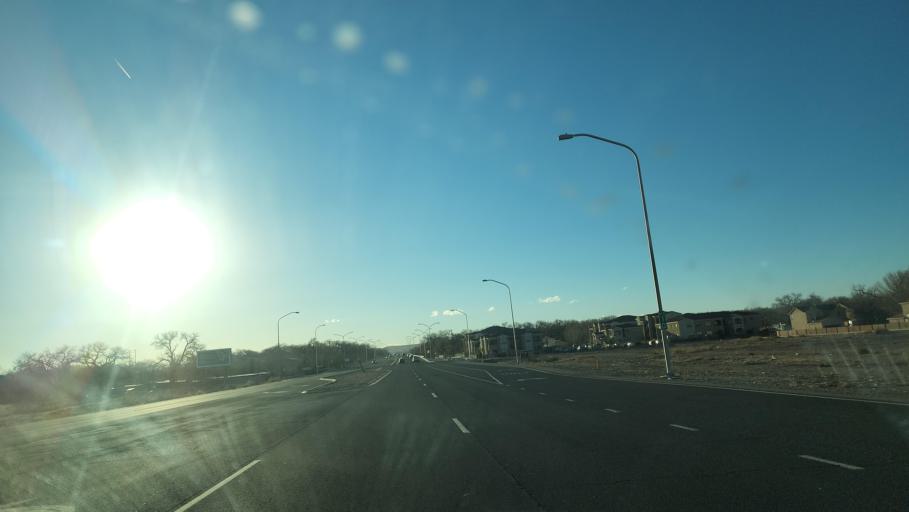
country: US
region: New Mexico
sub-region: Bernalillo County
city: South Valley
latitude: 35.0273
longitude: -106.6639
